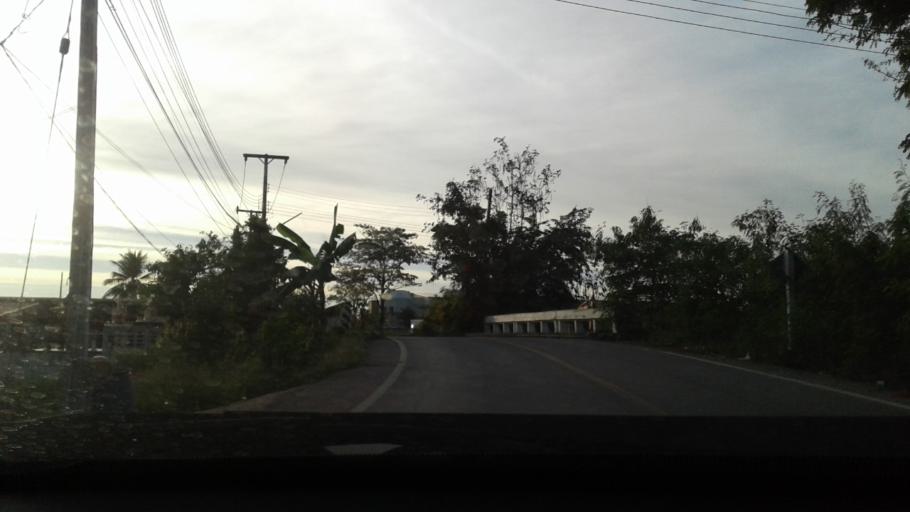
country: TH
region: Nonthaburi
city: Sai Noi
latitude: 13.9040
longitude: 100.2565
